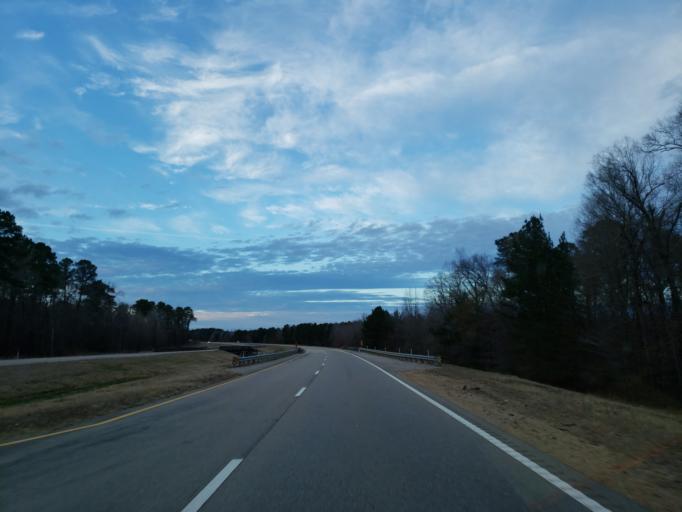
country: US
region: Mississippi
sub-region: Kemper County
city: De Kalb
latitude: 32.8007
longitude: -88.4546
